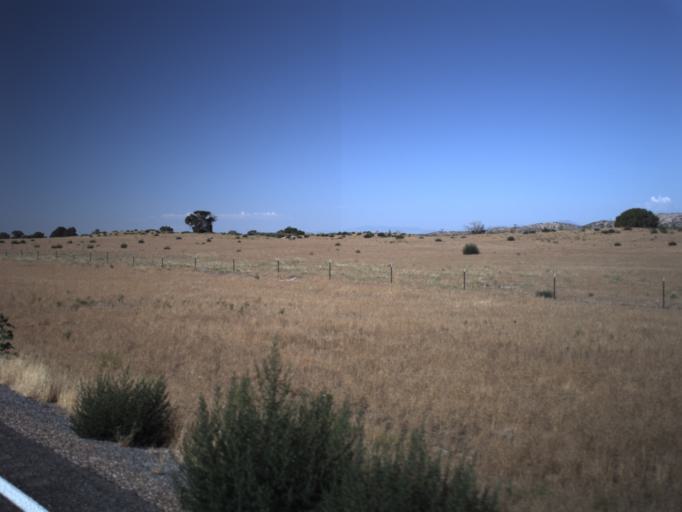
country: US
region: Utah
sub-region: Millard County
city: Delta
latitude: 39.6342
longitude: -112.3077
